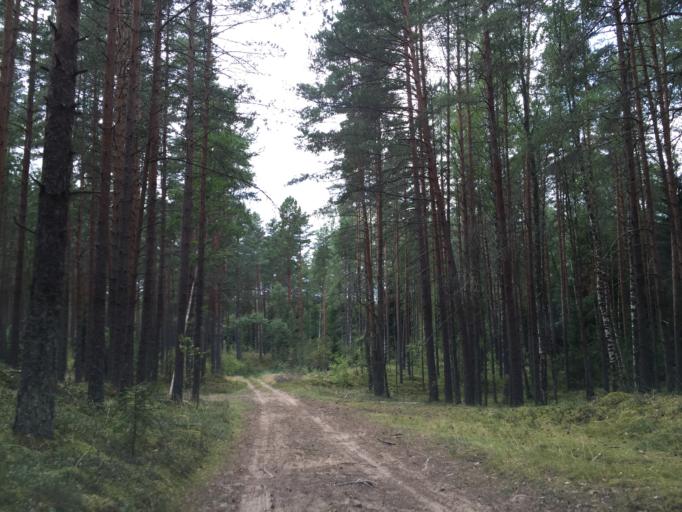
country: LV
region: Jurmala
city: Jurmala
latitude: 56.8715
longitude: 23.7065
